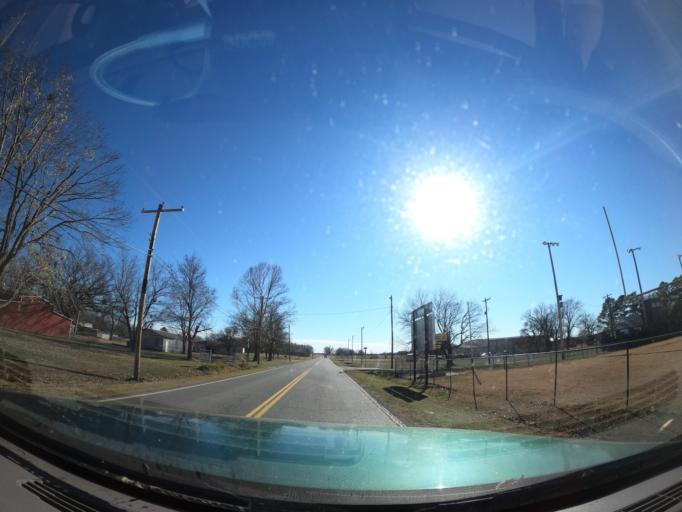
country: US
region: Oklahoma
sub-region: McIntosh County
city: Checotah
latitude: 35.5540
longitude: -95.6515
